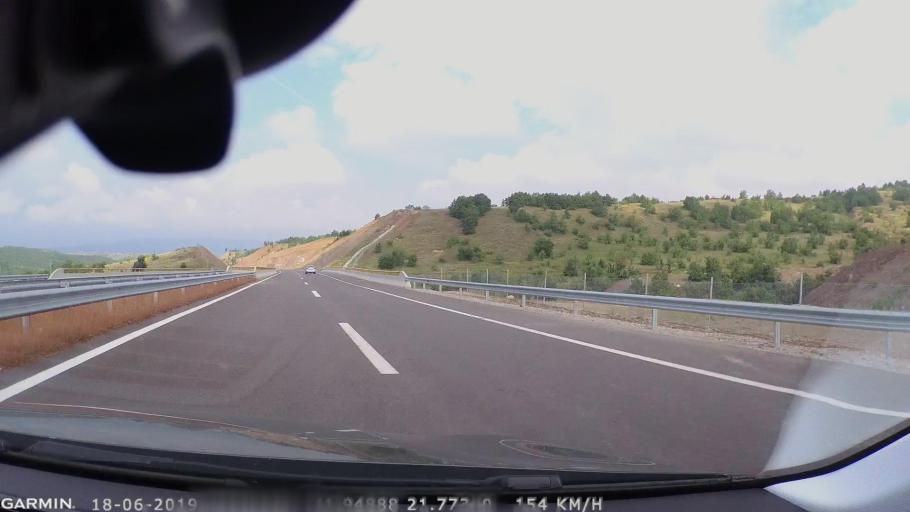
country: MK
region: Sveti Nikole
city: Gorobinci
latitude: 41.9235
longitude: 21.8478
